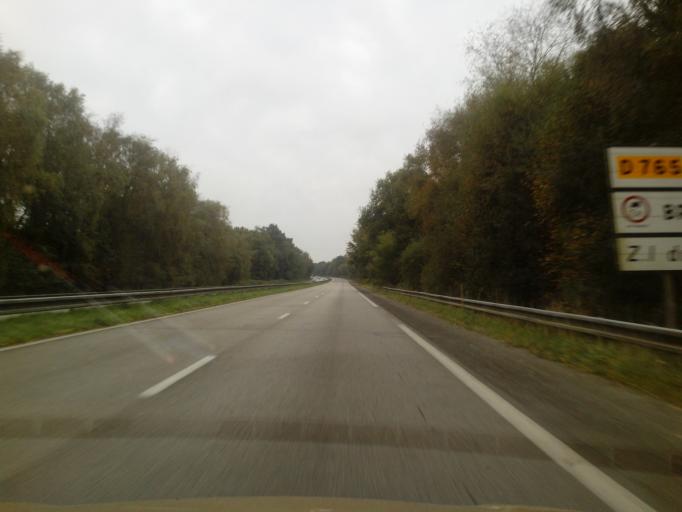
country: FR
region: Brittany
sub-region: Departement du Morbihan
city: Branderion
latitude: 47.8062
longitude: -3.2329
